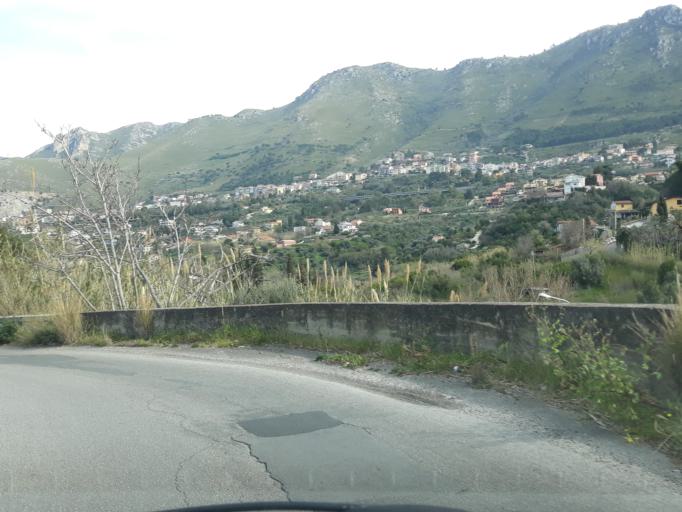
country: IT
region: Sicily
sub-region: Palermo
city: Piano Maglio-Blandino
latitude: 38.0666
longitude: 13.3041
